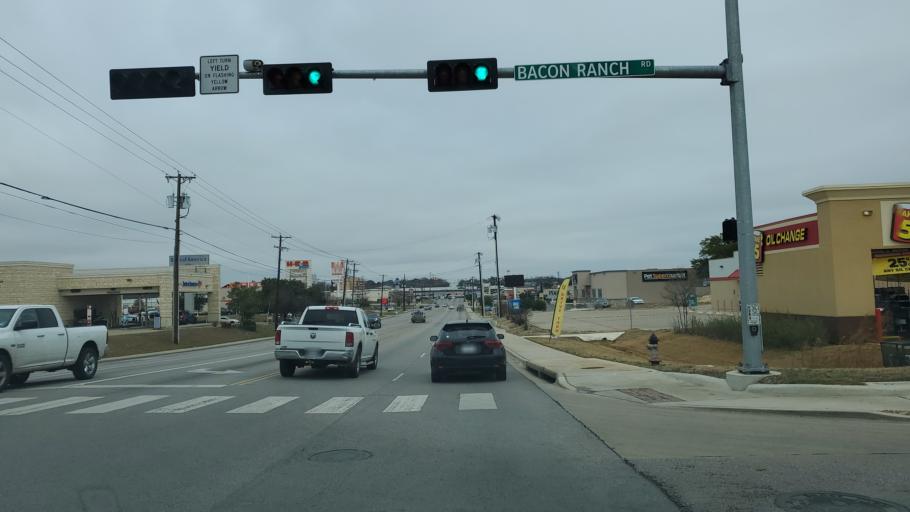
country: US
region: Texas
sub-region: Bell County
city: Killeen
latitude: 31.0898
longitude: -97.7341
